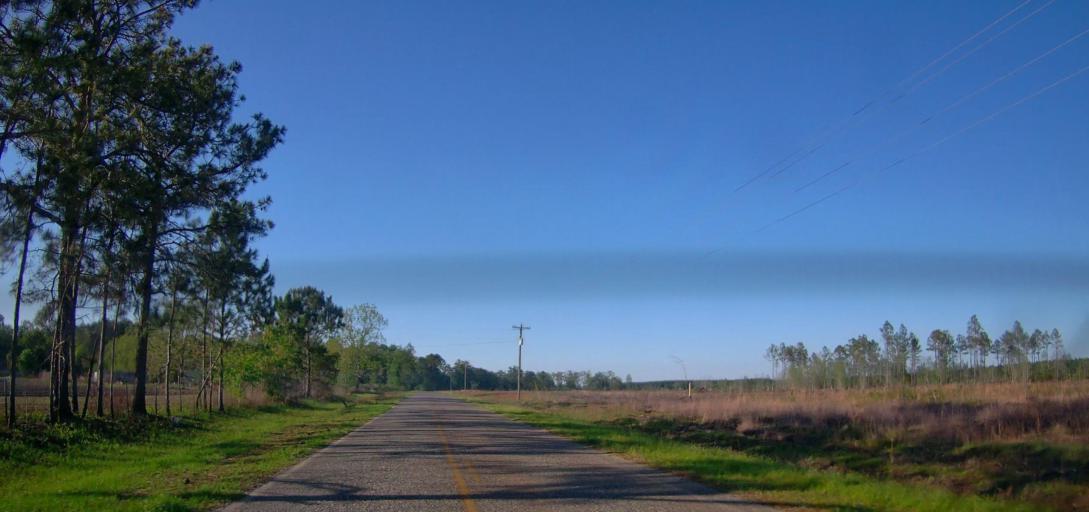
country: US
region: Georgia
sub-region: Ben Hill County
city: Fitzgerald
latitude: 31.6800
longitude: -83.1466
